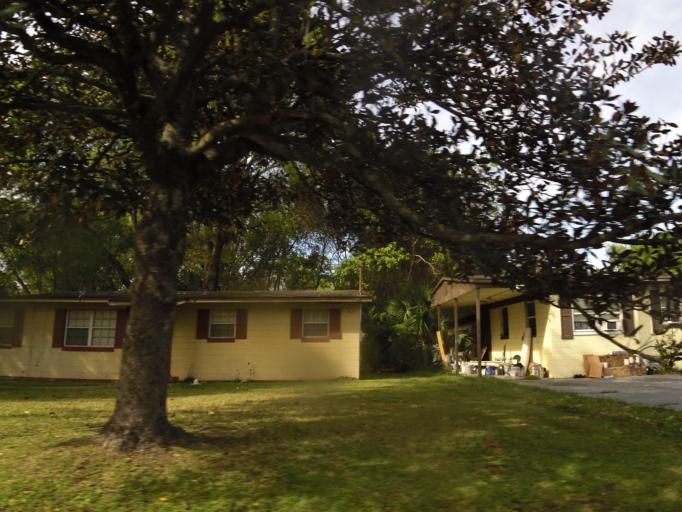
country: US
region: Florida
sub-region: Duval County
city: Jacksonville
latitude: 30.3032
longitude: -81.7343
